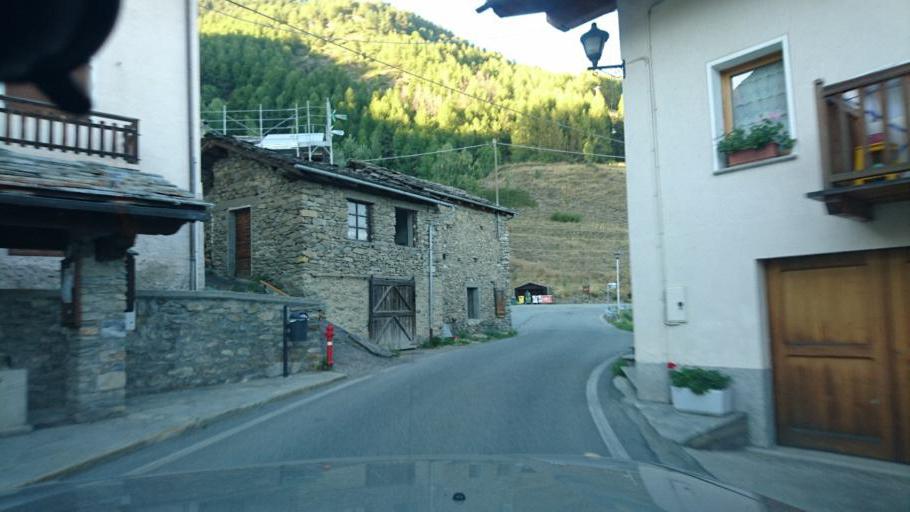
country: IT
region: Aosta Valley
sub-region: Valle d'Aosta
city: Avise
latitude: 45.7164
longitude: 7.1512
